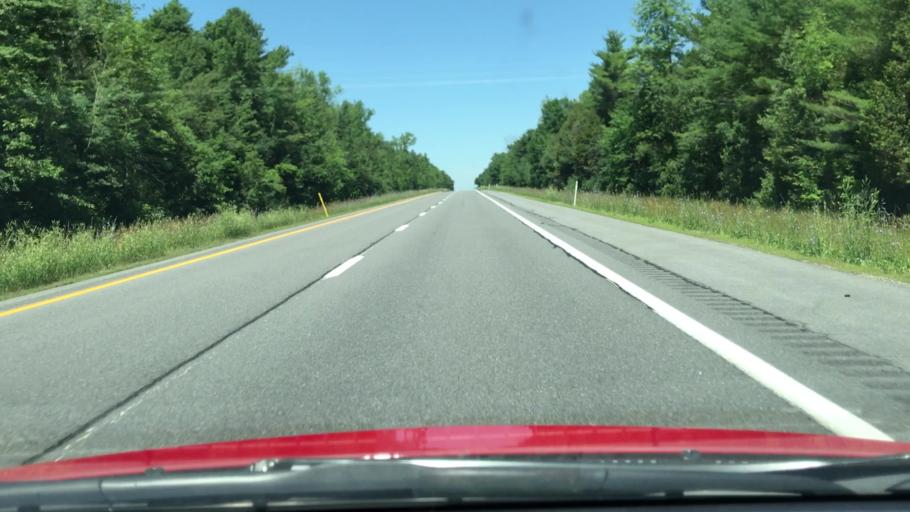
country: US
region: New York
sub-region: Clinton County
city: Champlain
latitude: 44.9558
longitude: -73.4487
